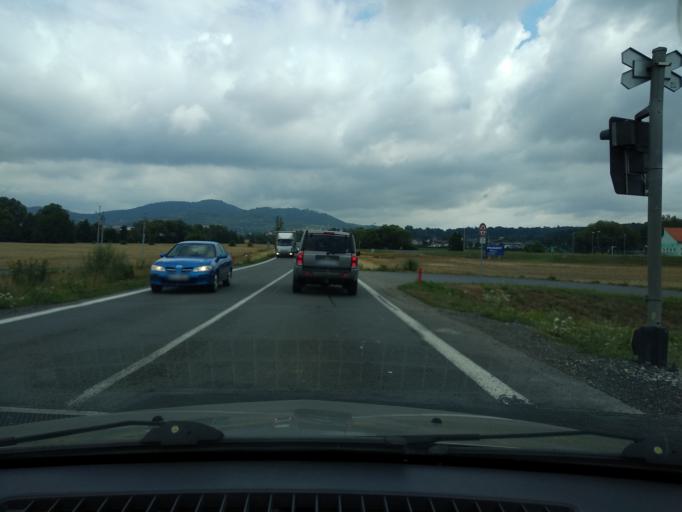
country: CZ
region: Olomoucky
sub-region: Okres Sumperk
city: Bludov
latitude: 49.9289
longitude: 16.9221
